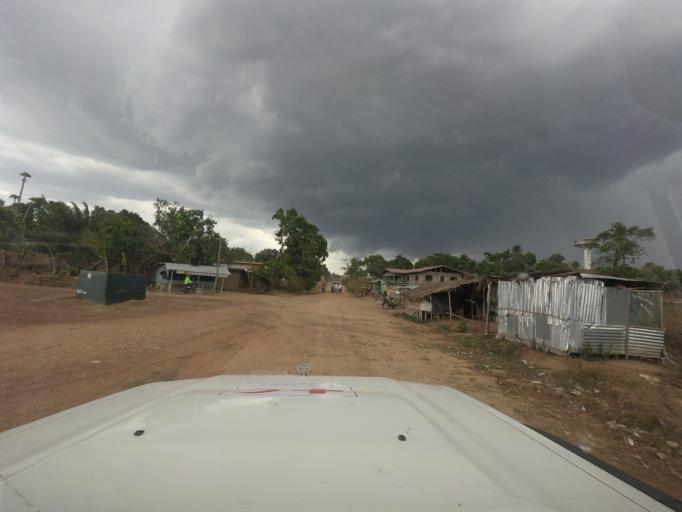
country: LR
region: Lofa
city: Voinjama
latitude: 8.4174
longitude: -9.7455
